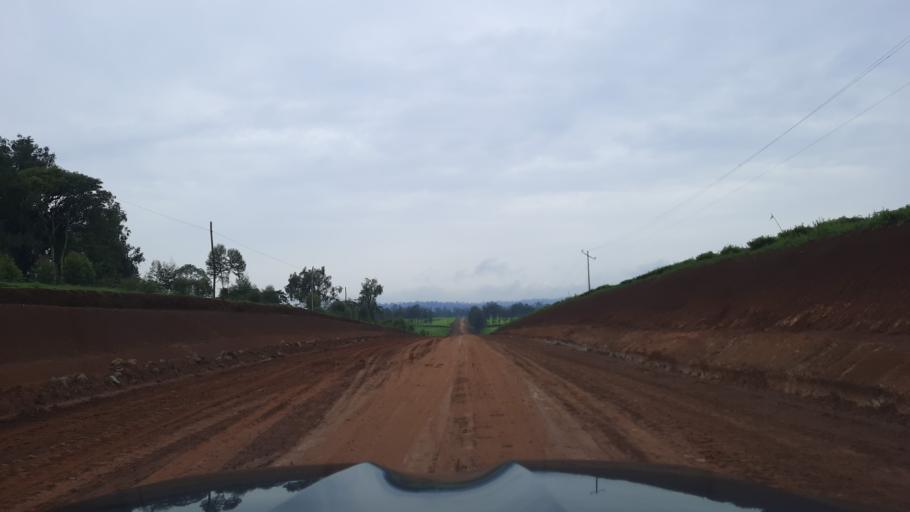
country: ET
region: Oromiya
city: Gore
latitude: 7.8455
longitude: 35.4768
